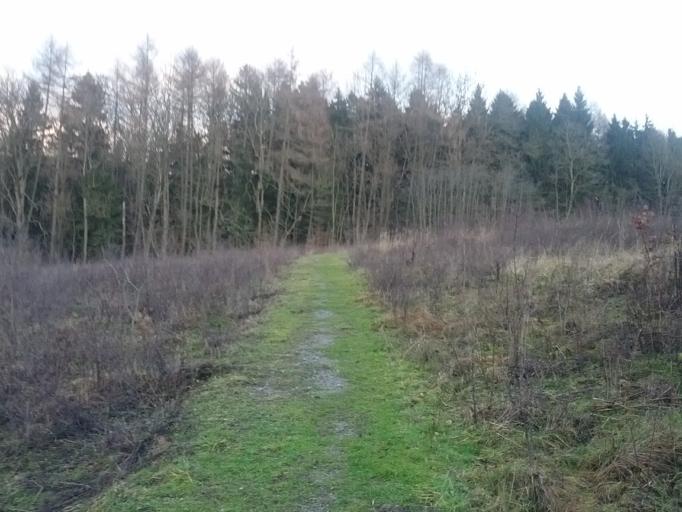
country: DE
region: Thuringia
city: Bischofroda
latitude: 51.0537
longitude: 10.4110
